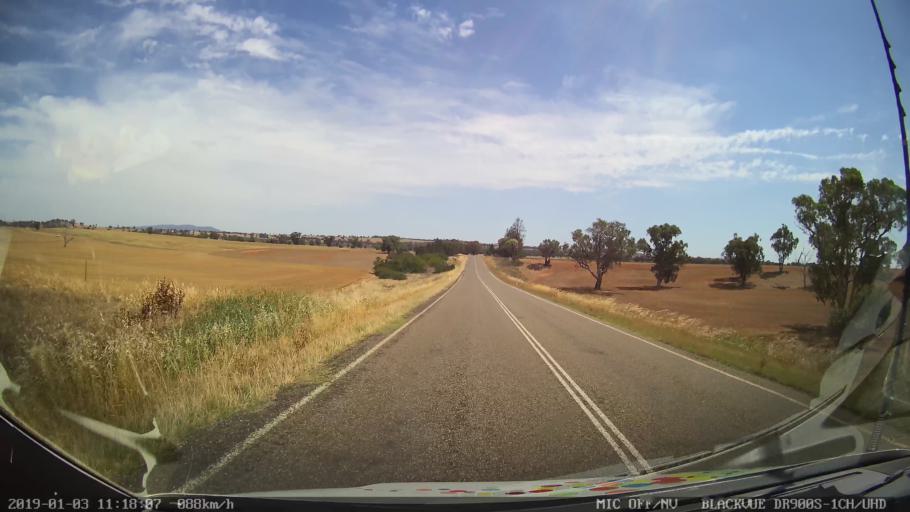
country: AU
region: New South Wales
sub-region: Young
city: Young
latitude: -34.1306
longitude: 148.2639
